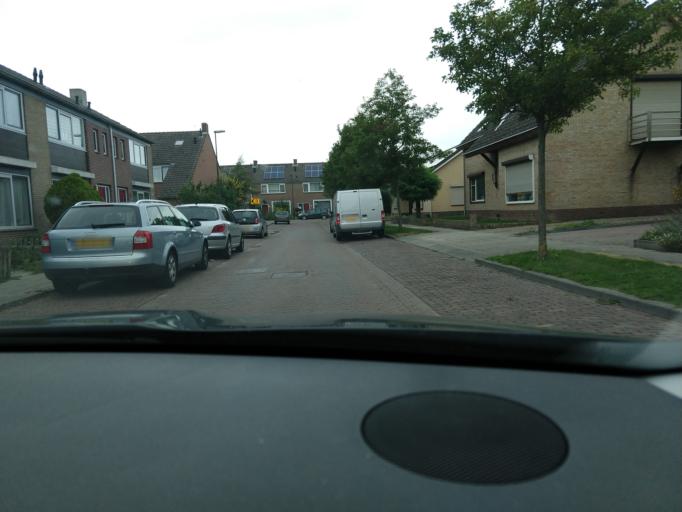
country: NL
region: Zeeland
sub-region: Gemeente Goes
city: Goes
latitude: 51.4335
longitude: 3.8796
